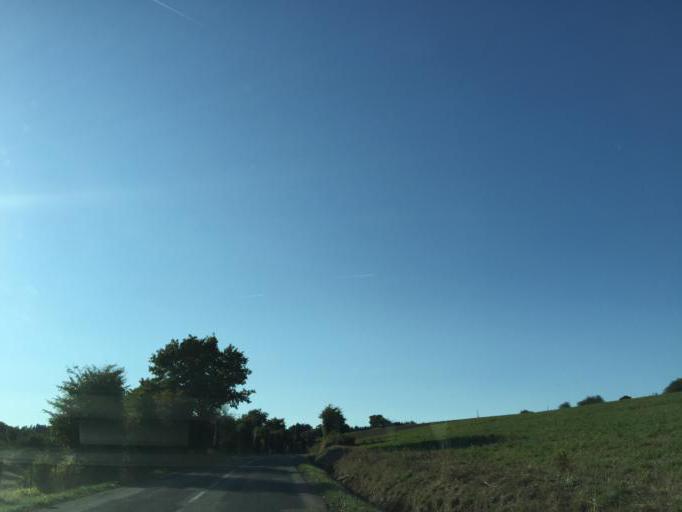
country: FR
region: Midi-Pyrenees
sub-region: Departement de l'Aveyron
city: Salles-Curan
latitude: 44.1296
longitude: 2.8898
